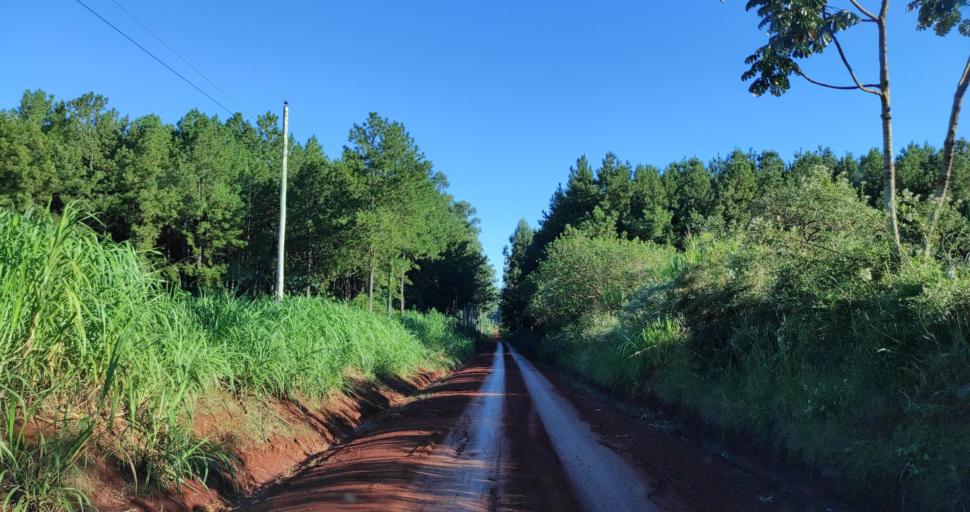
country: AR
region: Misiones
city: Puerto Rico
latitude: -26.8601
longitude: -55.0146
